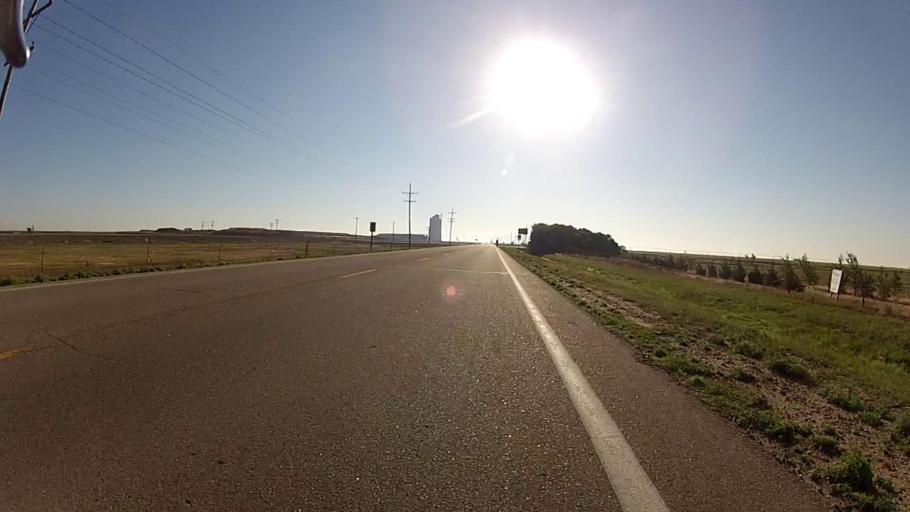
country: US
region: Kansas
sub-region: Haskell County
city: Sublette
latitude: 37.4851
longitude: -100.8368
